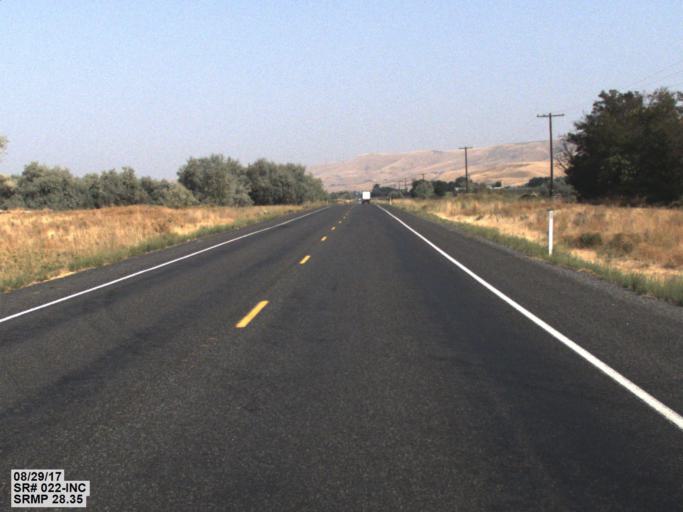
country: US
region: Washington
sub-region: Yakima County
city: Grandview
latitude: 46.1895
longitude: -119.8956
